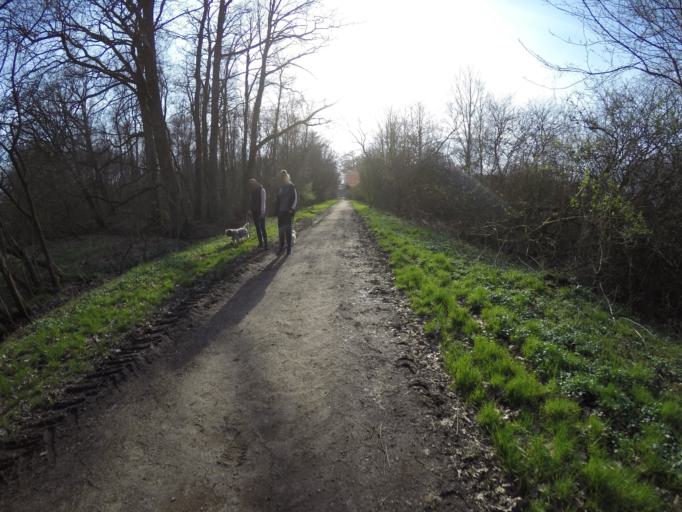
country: DE
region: Schleswig-Holstein
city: Bilsen
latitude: 53.7511
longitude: 9.8651
